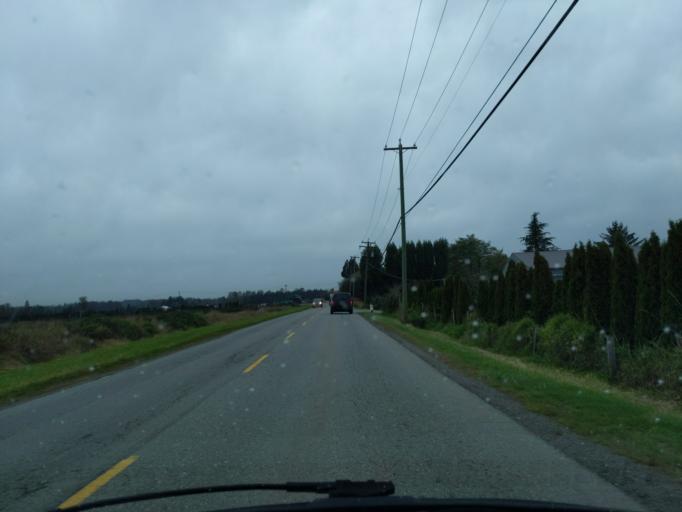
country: CA
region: British Columbia
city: Pitt Meadows
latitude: 49.2226
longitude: -122.7184
